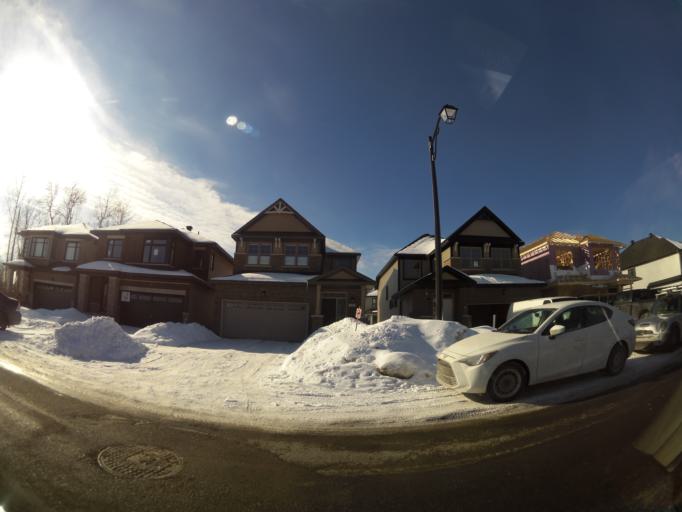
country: CA
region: Ontario
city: Ottawa
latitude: 45.4348
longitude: -75.5098
